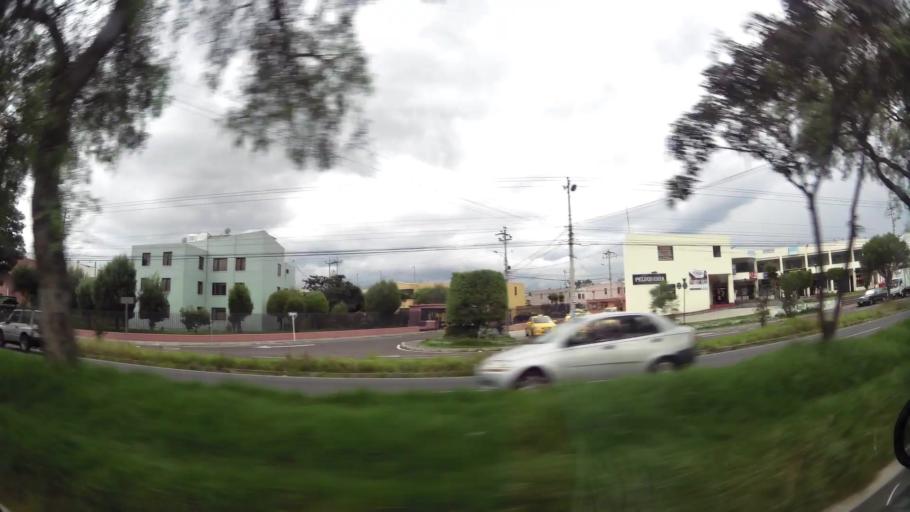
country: EC
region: Pichincha
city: Quito
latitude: -0.0694
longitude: -78.4697
